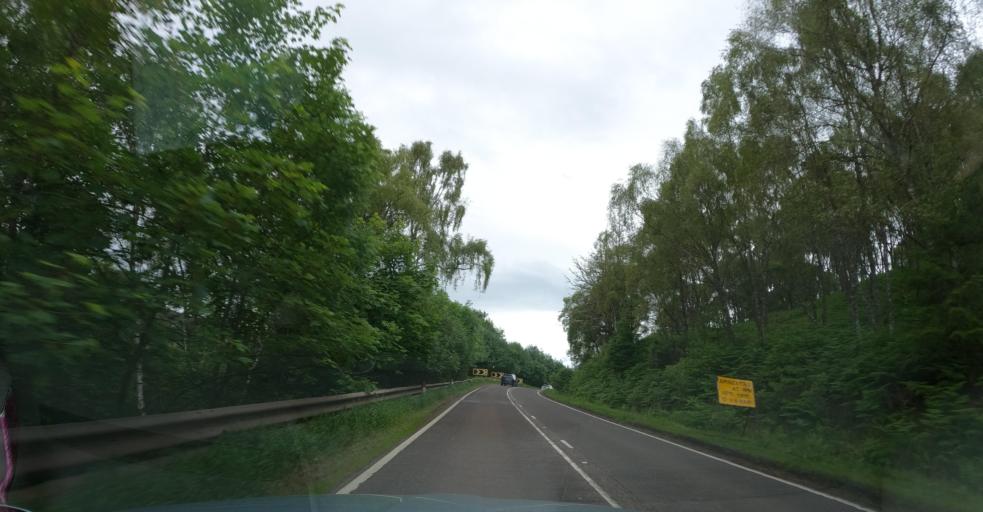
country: GB
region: Scotland
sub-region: Highland
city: Muir of Ord
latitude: 57.5936
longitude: -4.6453
